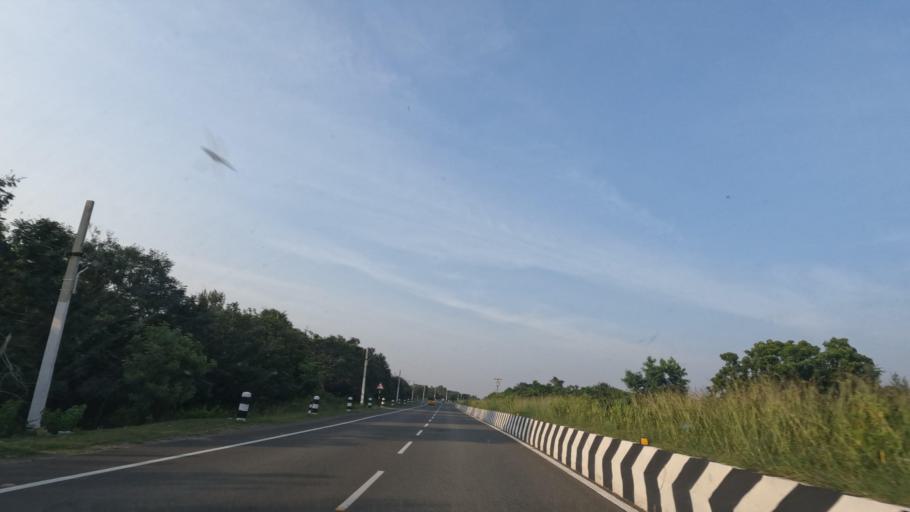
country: IN
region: Tamil Nadu
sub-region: Kancheepuram
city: Mamallapuram
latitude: 12.6722
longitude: 80.2114
